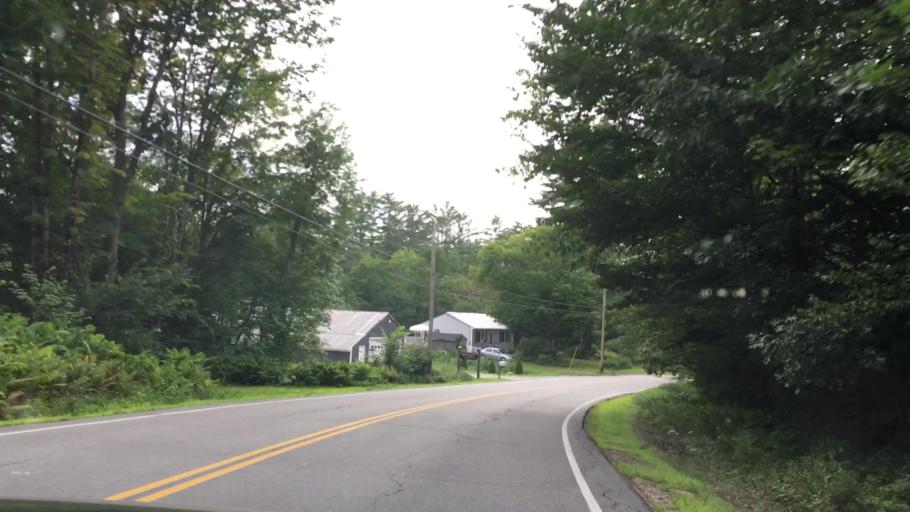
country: US
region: New Hampshire
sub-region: Carroll County
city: Center Harbor
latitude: 43.7046
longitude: -71.4970
